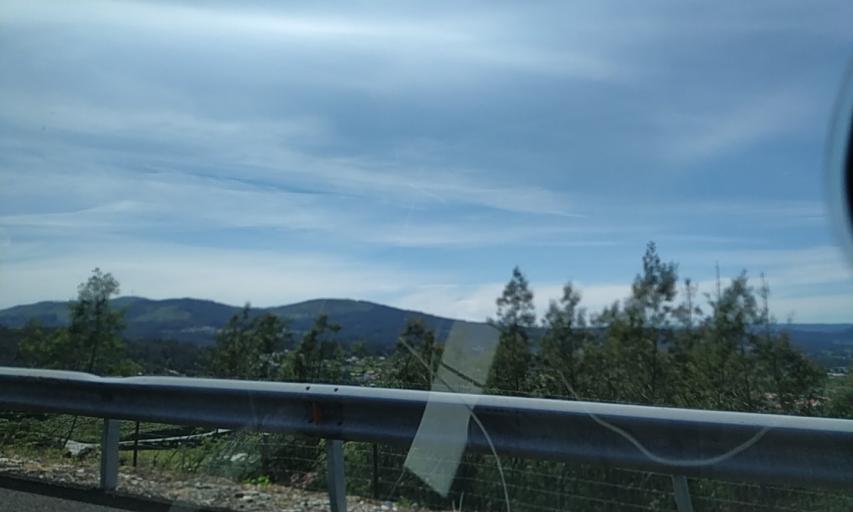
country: ES
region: Galicia
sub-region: Provincia de Pontevedra
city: Valga
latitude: 42.7005
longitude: -8.6373
